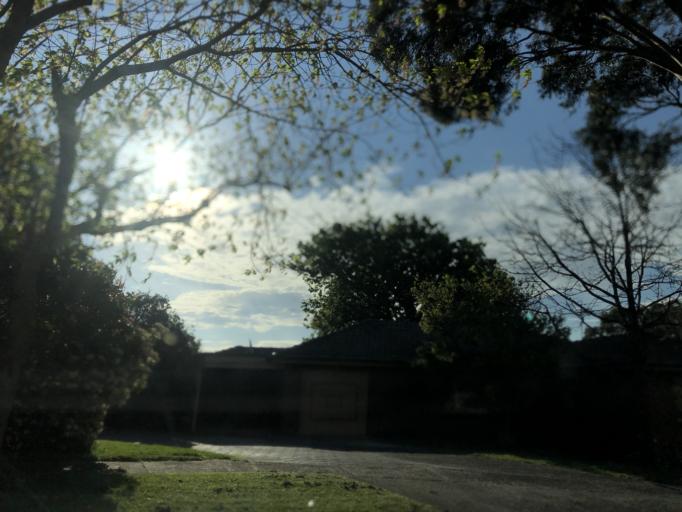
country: AU
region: Victoria
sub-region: Monash
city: Notting Hill
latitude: -37.8994
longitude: 145.1562
